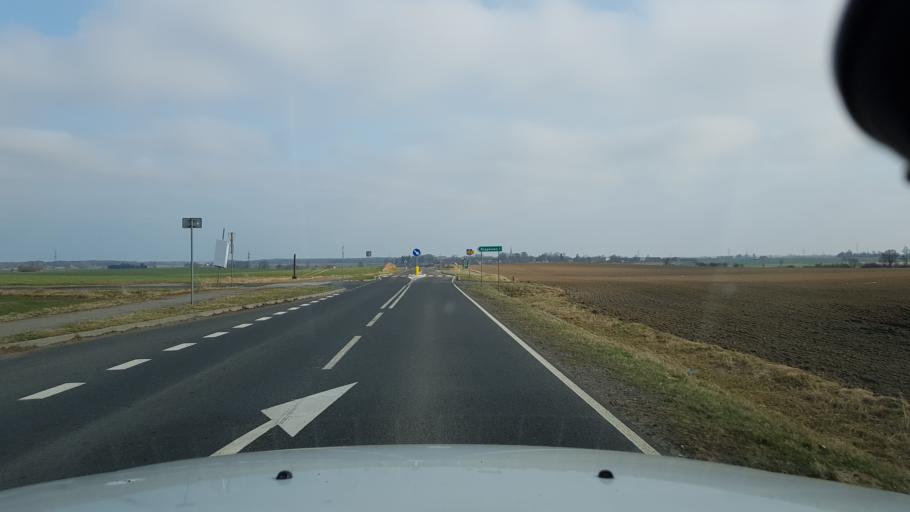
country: PL
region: West Pomeranian Voivodeship
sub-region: Powiat koszalinski
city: Sianow
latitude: 54.2806
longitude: 16.2703
